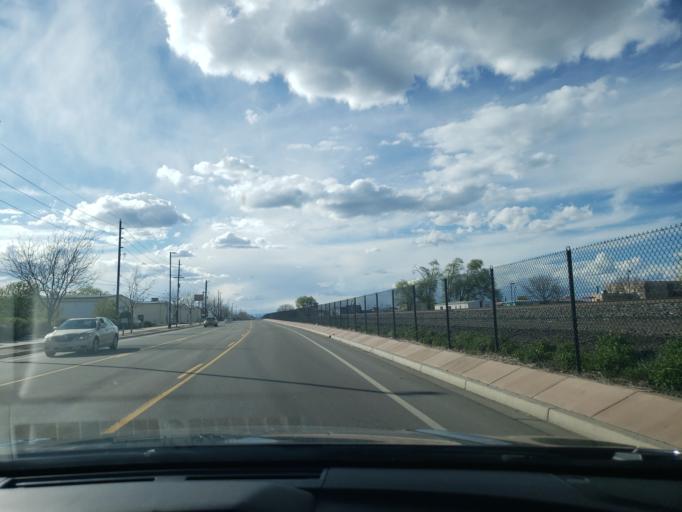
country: US
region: Colorado
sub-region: Mesa County
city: Redlands
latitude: 39.0821
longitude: -108.5918
